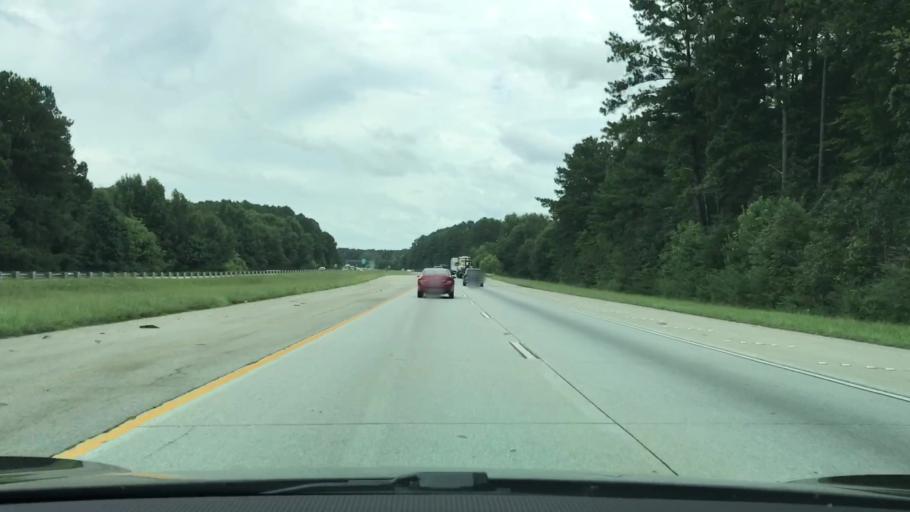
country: US
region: Georgia
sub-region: Coweta County
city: Grantville
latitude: 33.2159
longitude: -84.8202
